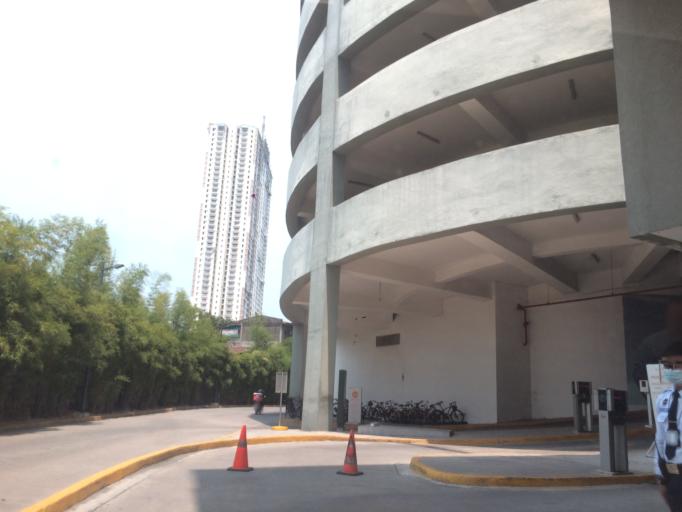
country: PH
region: Calabarzon
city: Del Monte
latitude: 14.6546
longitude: 121.0009
